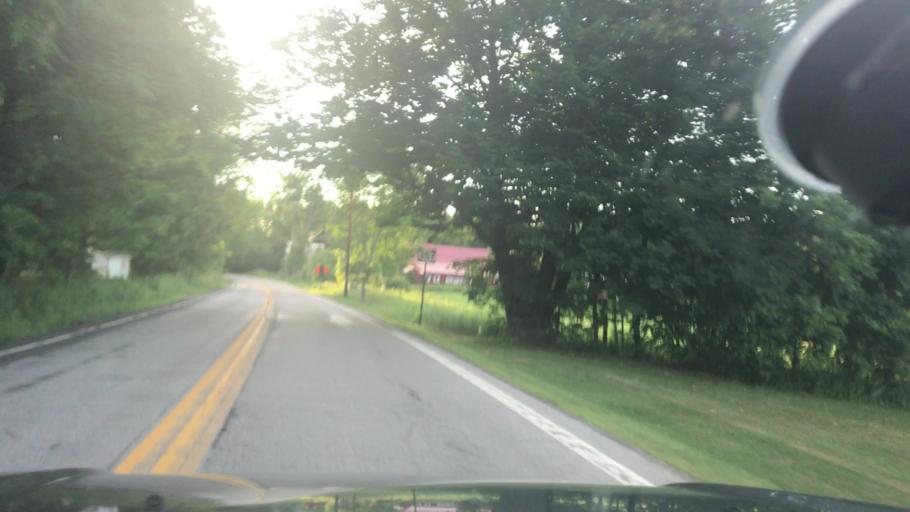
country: US
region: New York
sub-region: Otsego County
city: Unadilla
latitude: 42.3343
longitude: -75.2371
